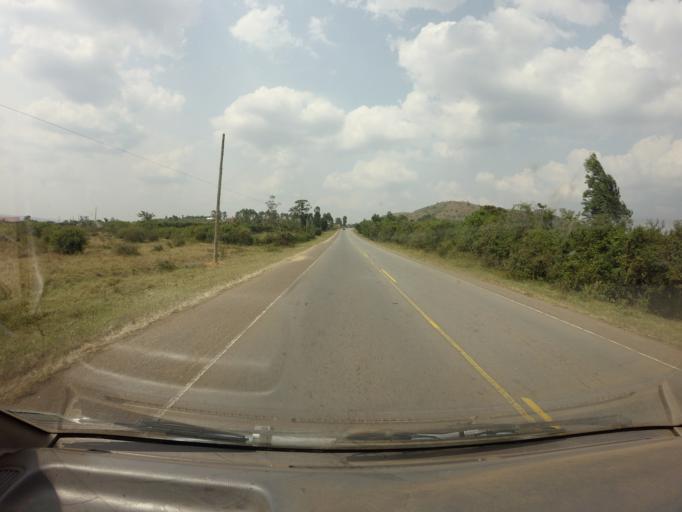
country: UG
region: Central Region
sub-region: Lyantonde District
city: Lyantonde
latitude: -0.3935
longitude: 31.1802
